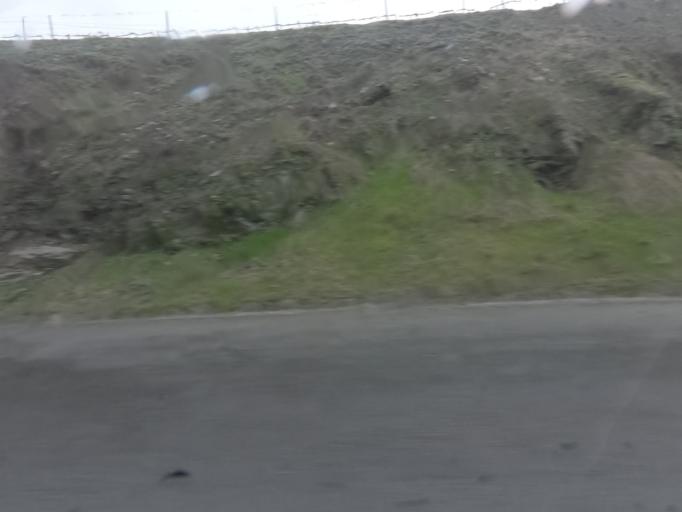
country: PT
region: Vila Real
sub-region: Peso da Regua
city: Peso da Regua
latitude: 41.1722
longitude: -7.7625
